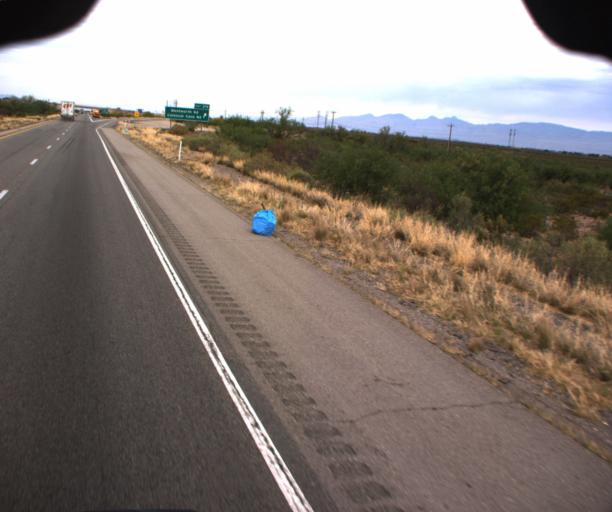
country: US
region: Arizona
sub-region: Pima County
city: Vail
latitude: 32.0251
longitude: -110.7158
